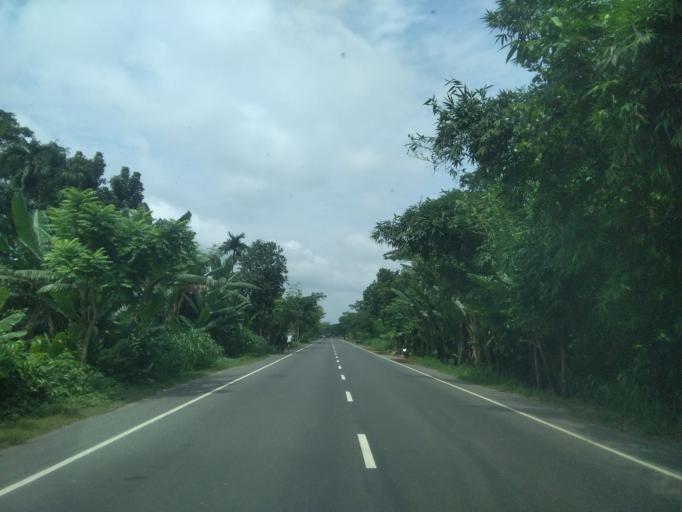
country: BD
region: Khulna
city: Kesabpur
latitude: 22.8028
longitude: 89.2338
